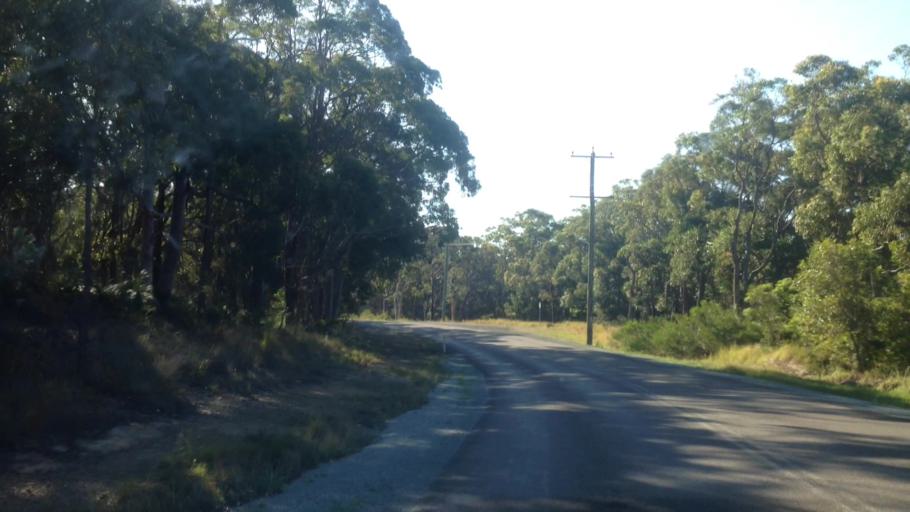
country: AU
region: New South Wales
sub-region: Lake Macquarie Shire
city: Arcadia vale
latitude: -33.1111
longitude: 151.5610
